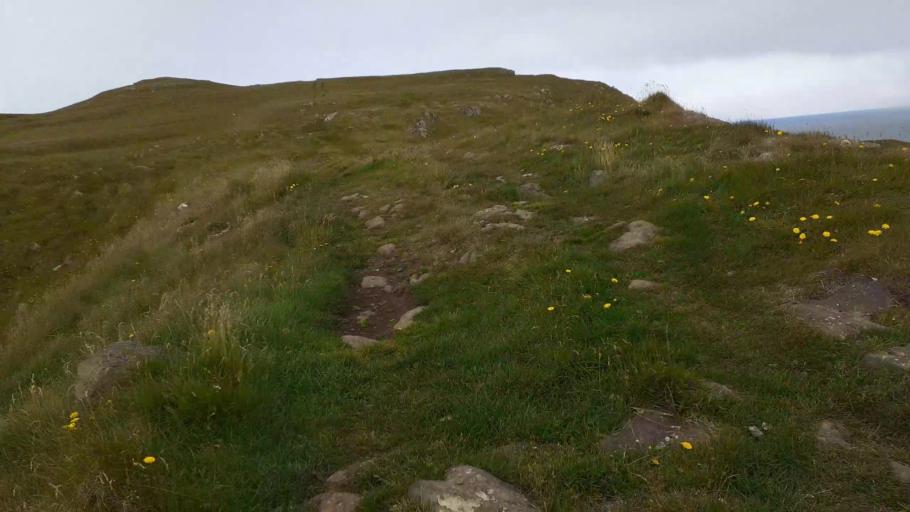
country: IS
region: Northeast
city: Dalvik
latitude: 66.5328
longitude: -17.9827
